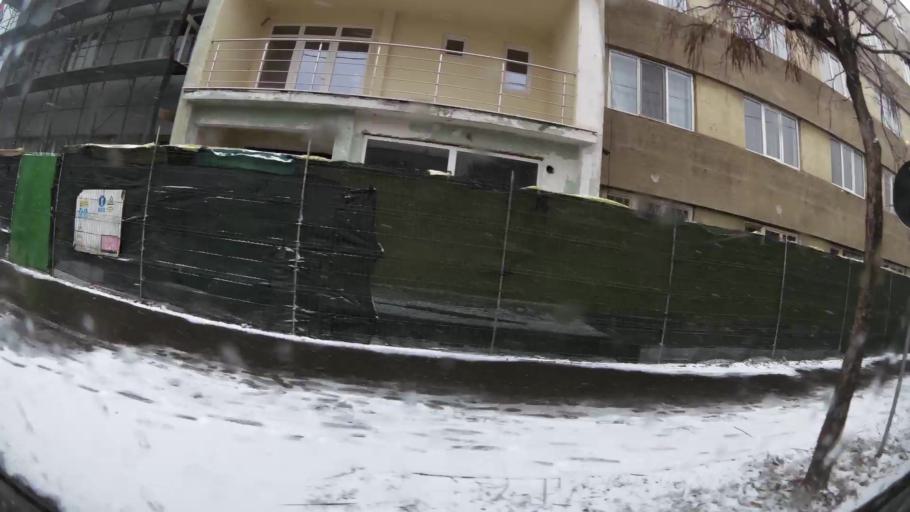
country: RO
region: Dambovita
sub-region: Municipiul Targoviste
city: Targoviste
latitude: 44.9189
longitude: 25.4612
